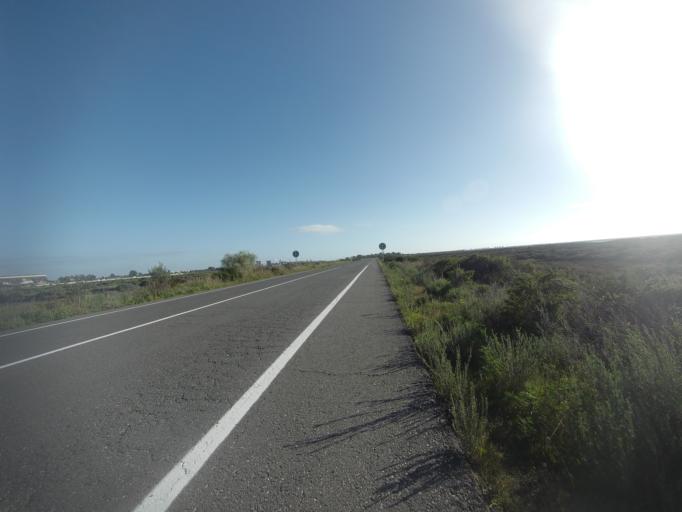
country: ES
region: Andalusia
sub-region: Provincia de Huelva
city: Huelva
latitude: 37.2485
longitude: -6.9676
